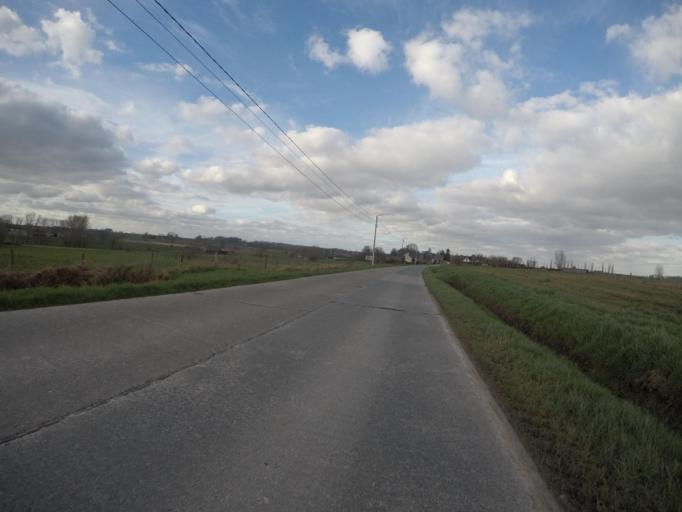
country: BE
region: Flanders
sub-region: Provincie Vlaams-Brabant
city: Pepingen
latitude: 50.7339
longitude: 4.1350
